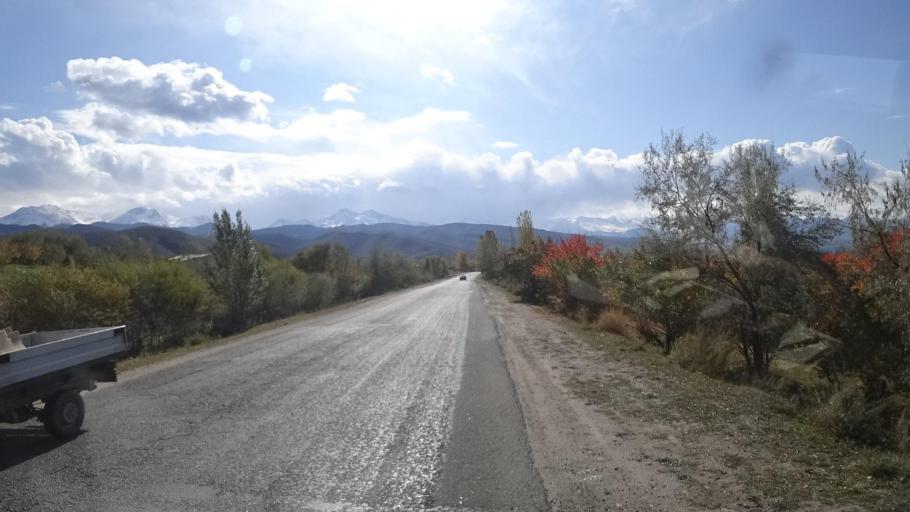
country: KG
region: Ysyk-Koel
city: Pokrovka
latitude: 42.2293
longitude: 77.7149
